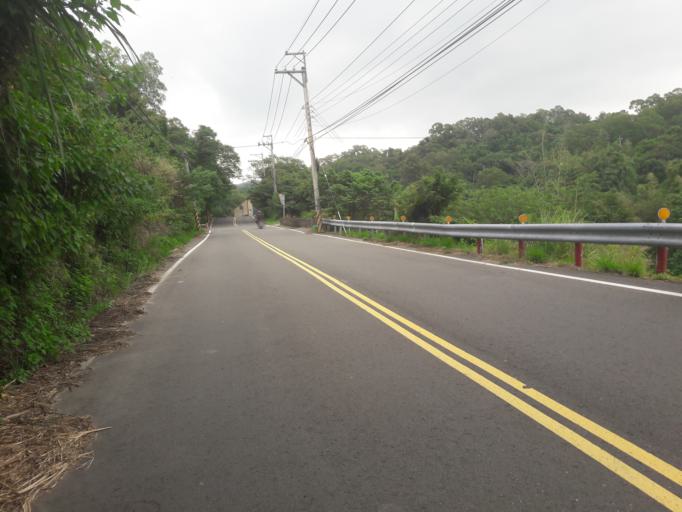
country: TW
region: Taiwan
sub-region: Hsinchu
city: Hsinchu
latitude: 24.7301
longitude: 120.9679
